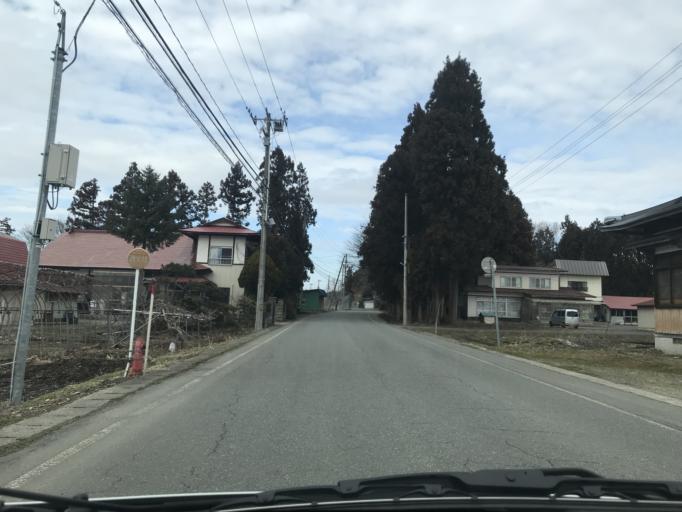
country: JP
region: Iwate
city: Kitakami
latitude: 39.3219
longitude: 140.9857
